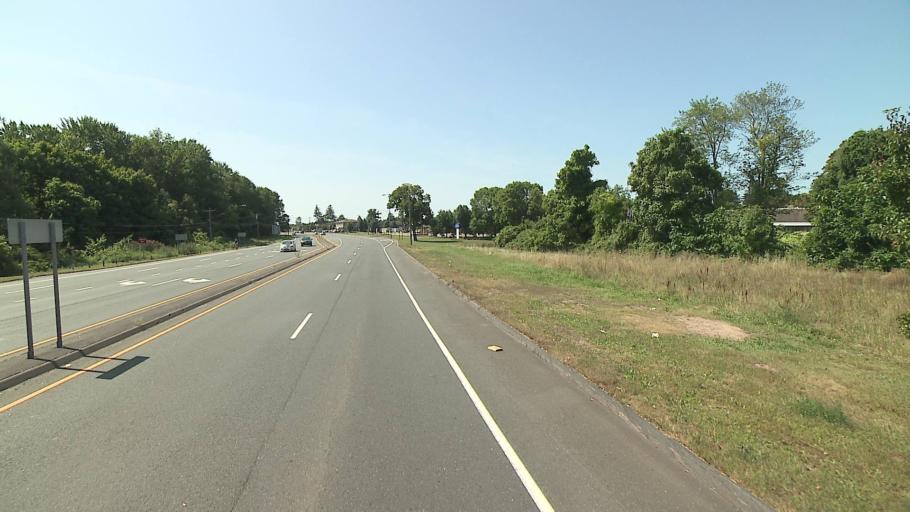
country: US
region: Connecticut
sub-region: Hartford County
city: Windsor Locks
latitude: 41.9167
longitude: -72.6117
